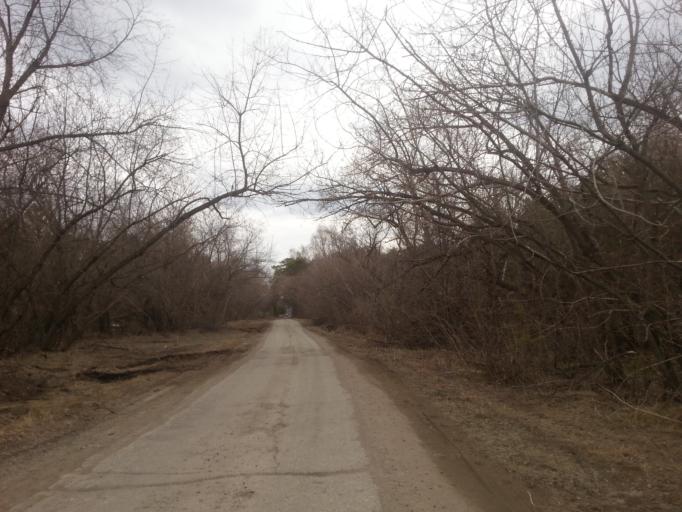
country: RU
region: Altai Krai
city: Yuzhnyy
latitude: 53.2863
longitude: 83.7305
